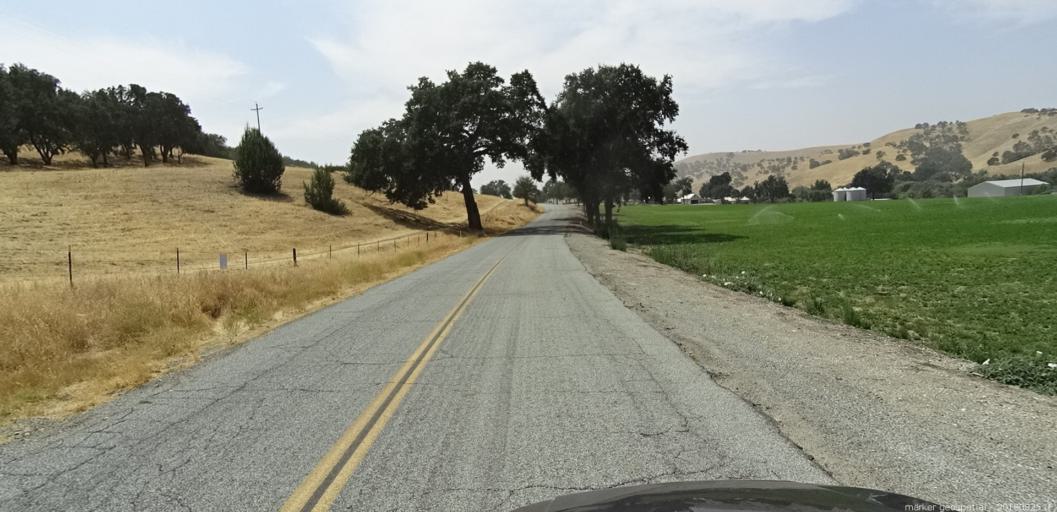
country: US
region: California
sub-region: San Luis Obispo County
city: San Miguel
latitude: 35.8110
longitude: -120.6686
